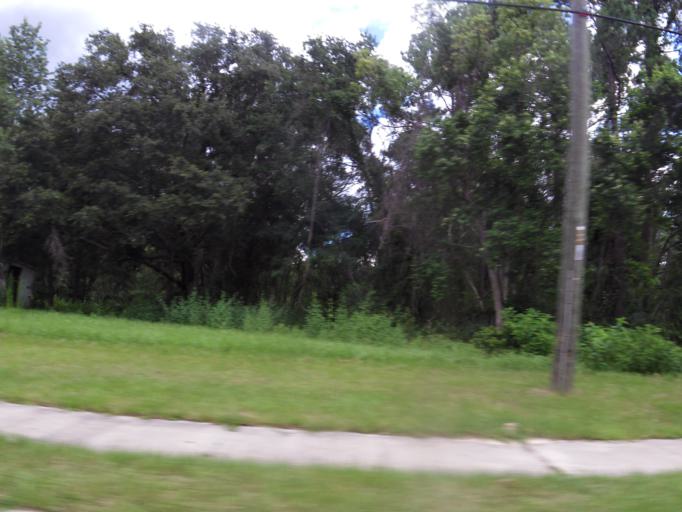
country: US
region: Florida
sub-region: Duval County
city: Jacksonville
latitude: 30.4141
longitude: -81.6606
